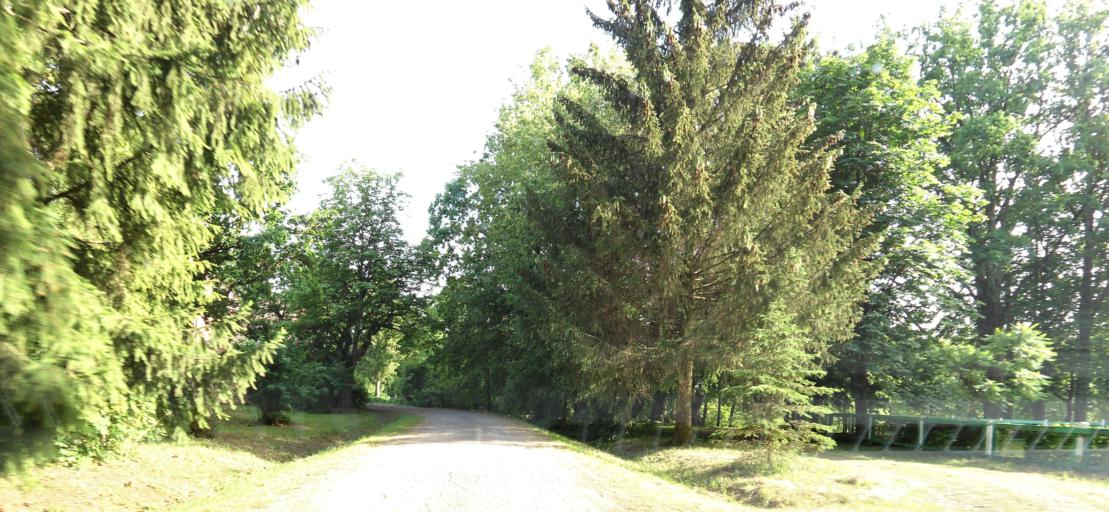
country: LT
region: Panevezys
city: Pasvalys
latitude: 56.1071
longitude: 24.4956
